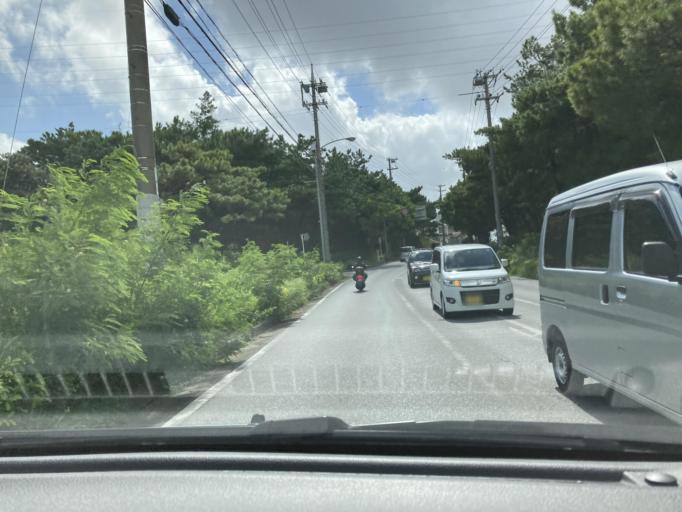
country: JP
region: Okinawa
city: Ginowan
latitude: 26.2573
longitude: 127.7243
